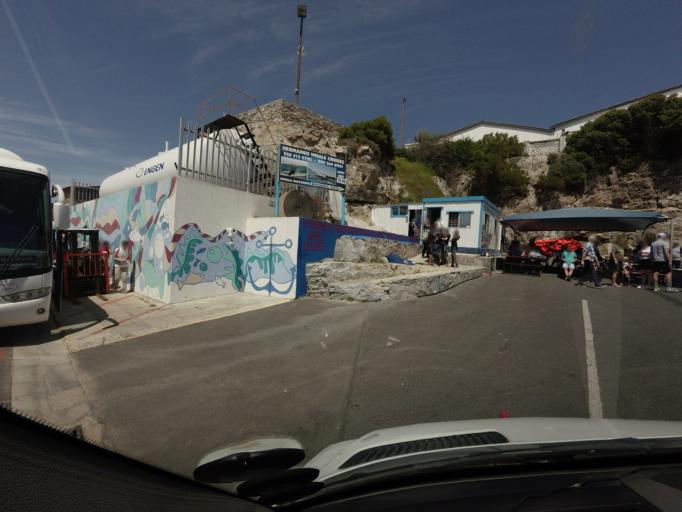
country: ZA
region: Western Cape
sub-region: Overberg District Municipality
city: Hermanus
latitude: -34.4339
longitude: 19.2246
